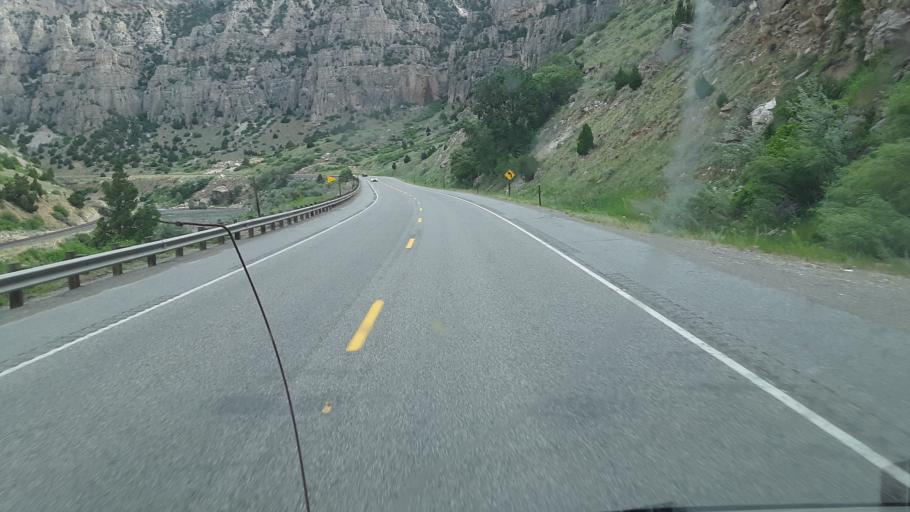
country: US
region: Wyoming
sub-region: Hot Springs County
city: Thermopolis
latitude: 43.5219
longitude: -108.1774
